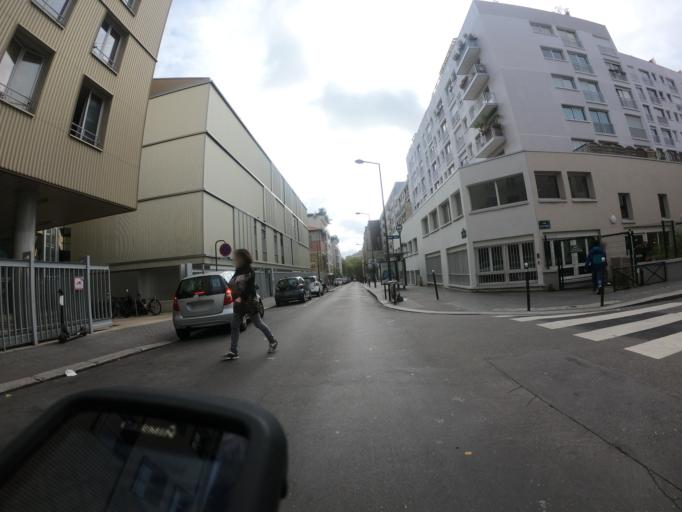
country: FR
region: Ile-de-France
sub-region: Departement du Val-de-Marne
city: Le Kremlin-Bicetre
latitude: 48.8254
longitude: 2.3510
